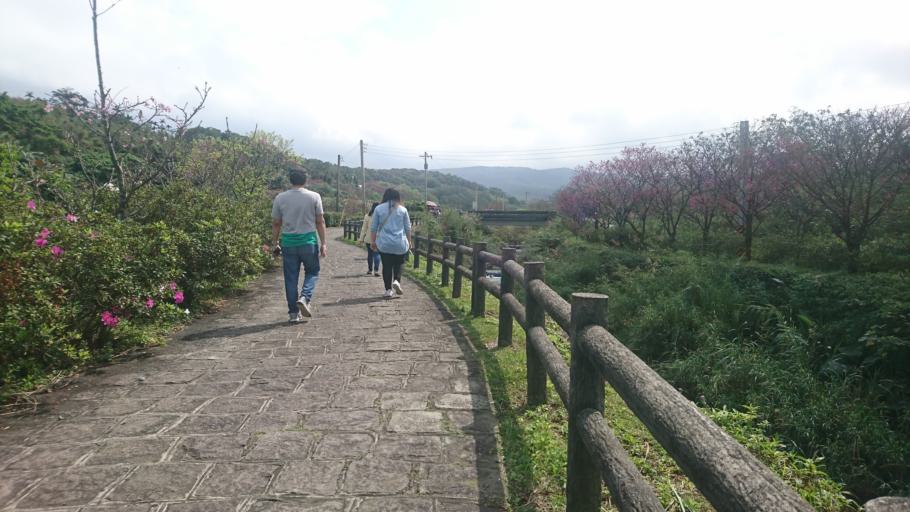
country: TW
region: Taipei
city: Taipei
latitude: 25.2663
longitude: 121.5125
